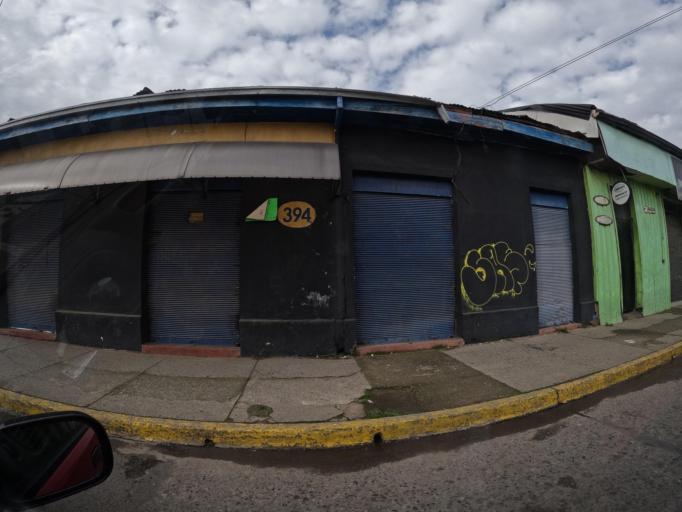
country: CL
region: Maule
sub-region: Provincia de Linares
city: Linares
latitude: -35.8488
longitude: -71.5919
